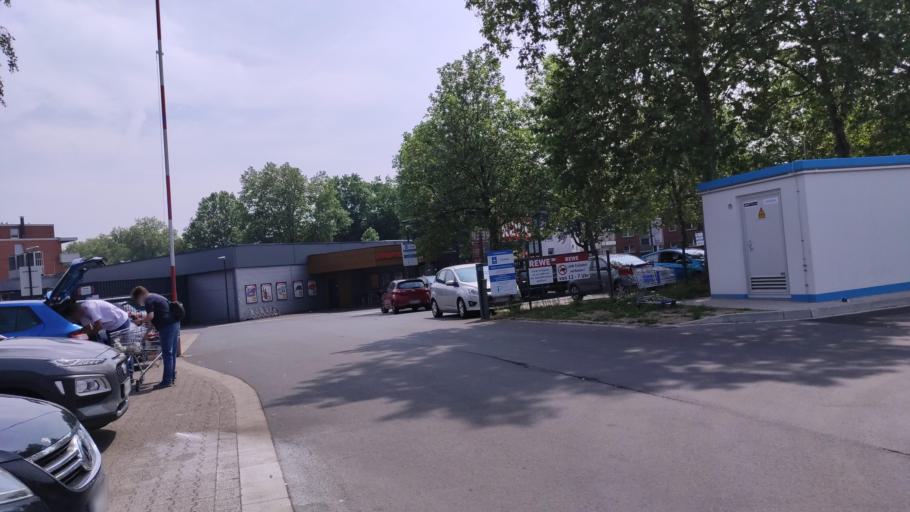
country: DE
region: North Rhine-Westphalia
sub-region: Regierungsbezirk Munster
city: Gelsenkirchen
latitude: 51.5199
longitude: 7.0825
